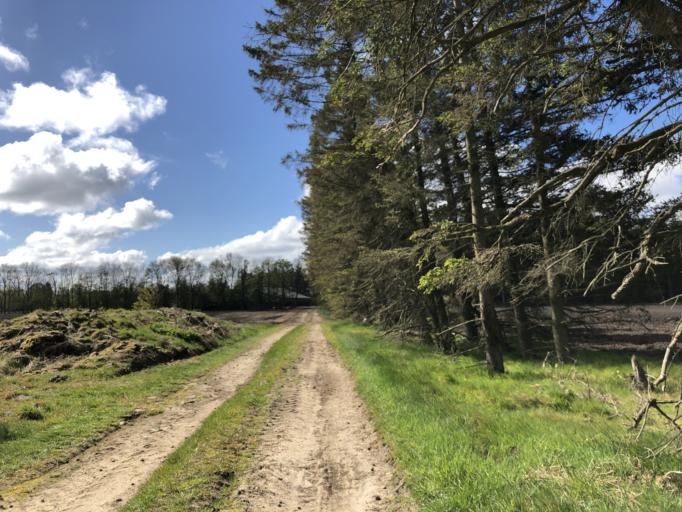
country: DK
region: Central Jutland
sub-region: Holstebro Kommune
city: Ulfborg
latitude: 56.2402
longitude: 8.4682
